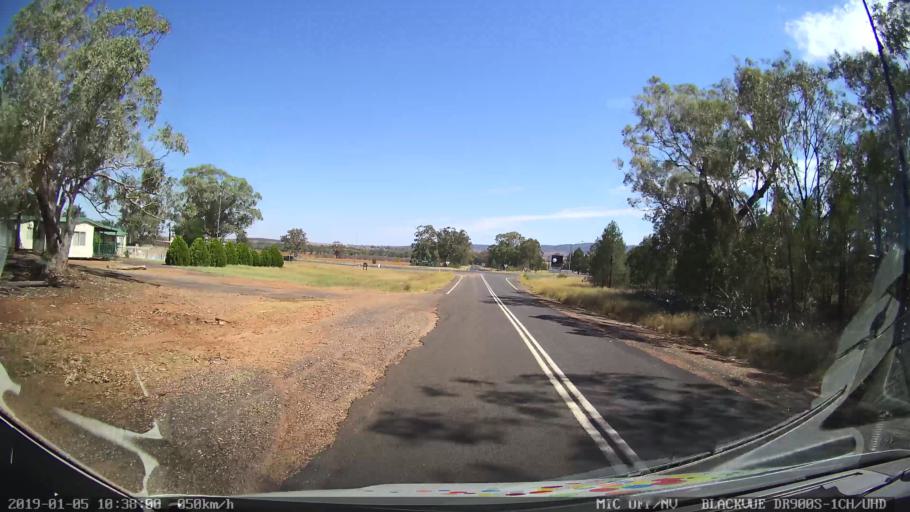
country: AU
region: New South Wales
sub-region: Gilgandra
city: Gilgandra
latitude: -31.4706
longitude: 148.9204
